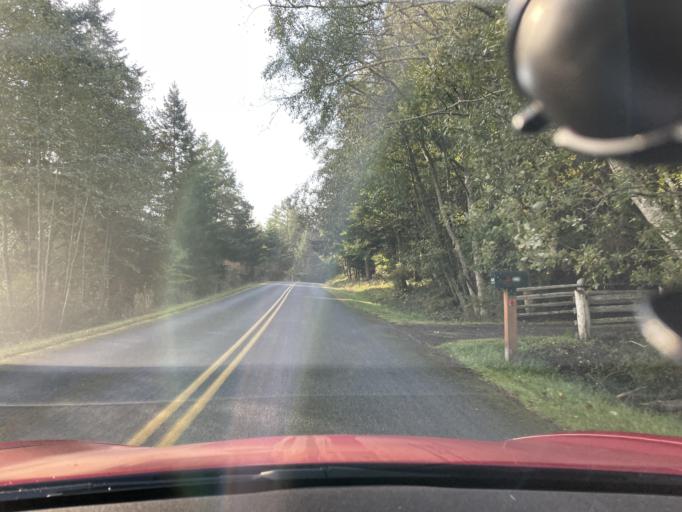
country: US
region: Washington
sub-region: San Juan County
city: Friday Harbor
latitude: 48.5595
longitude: -123.1645
